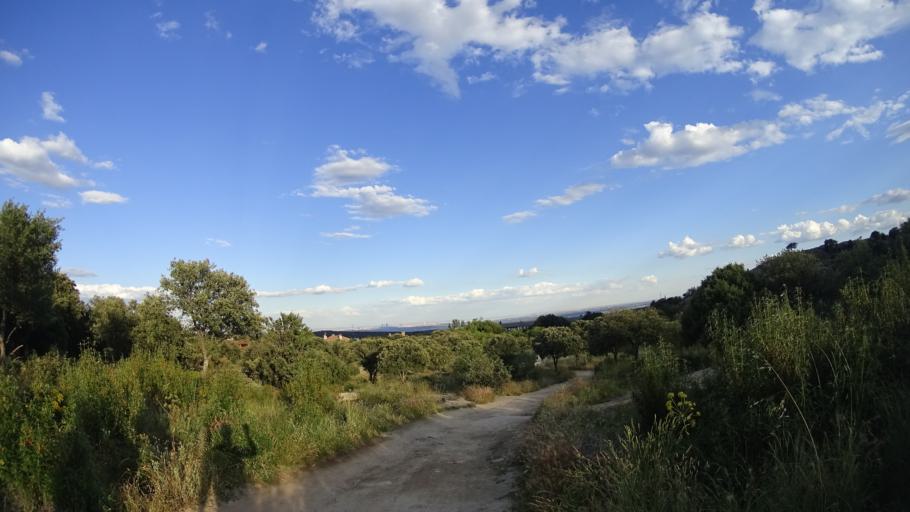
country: ES
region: Madrid
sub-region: Provincia de Madrid
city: Hoyo de Manzanares
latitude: 40.6268
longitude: -3.9161
